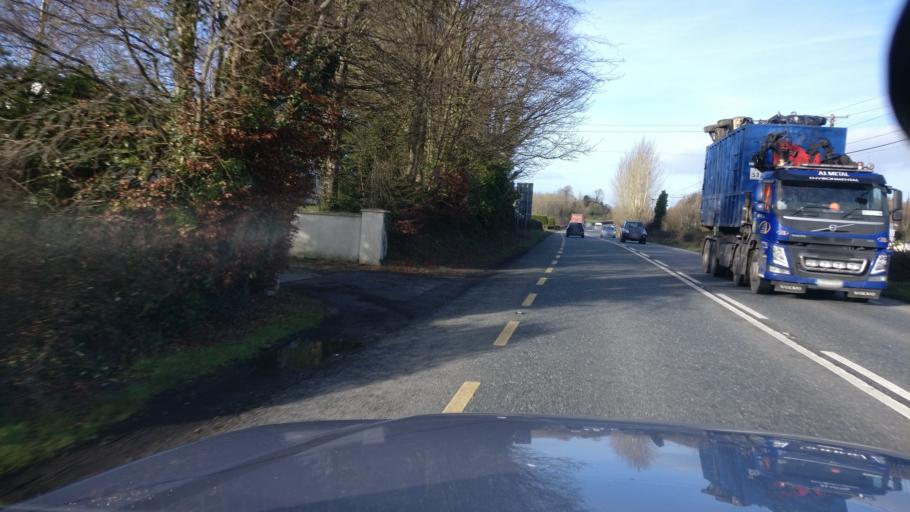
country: IE
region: Leinster
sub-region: Uibh Fhaili
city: Tullamore
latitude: 53.2248
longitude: -7.4759
